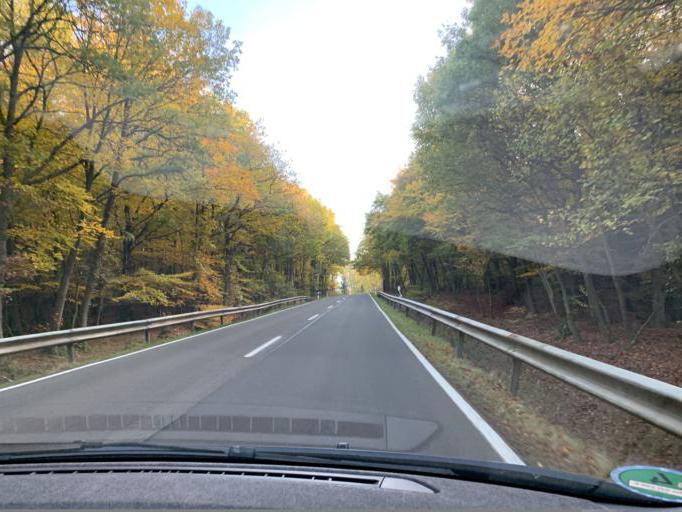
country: DE
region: North Rhine-Westphalia
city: Heimbach
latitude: 50.5996
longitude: 6.4900
